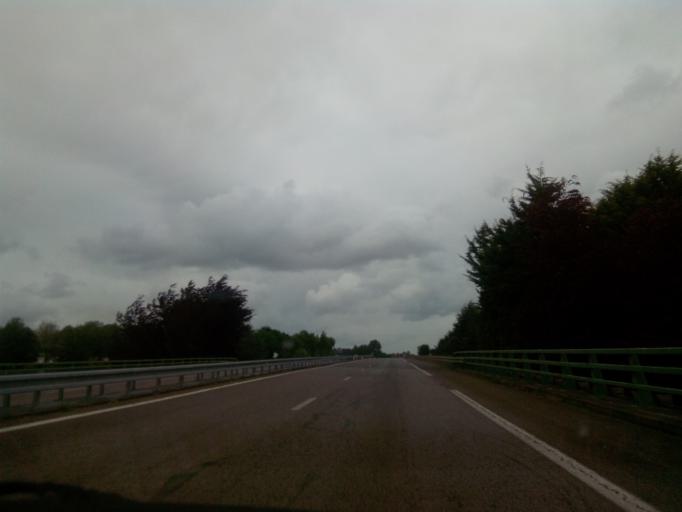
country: FR
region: Brittany
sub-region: Departement du Morbihan
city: Malestroit
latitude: 47.8513
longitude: -2.4198
